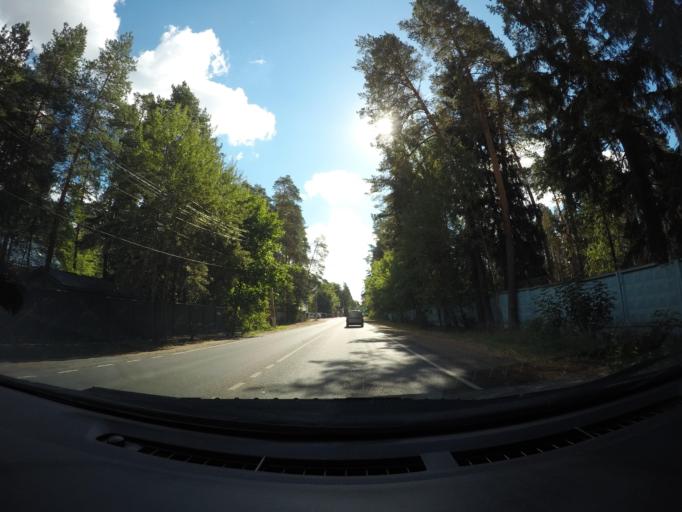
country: RU
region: Moskovskaya
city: Kratovo
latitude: 55.5989
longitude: 38.1773
